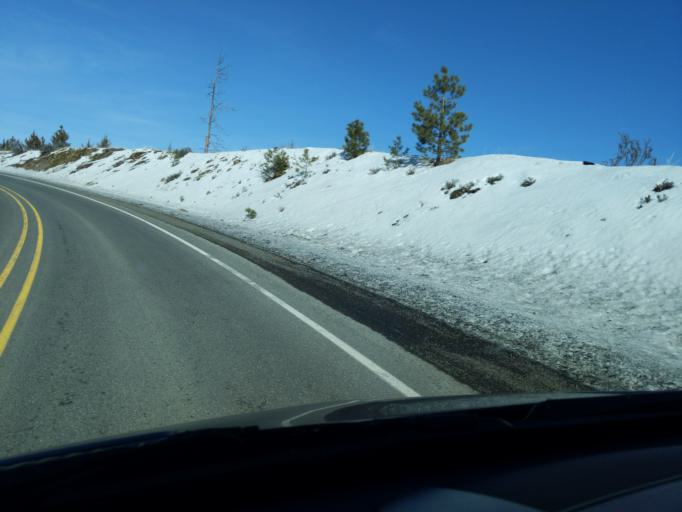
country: US
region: Oregon
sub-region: Grant County
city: John Day
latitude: 44.9084
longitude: -119.0094
